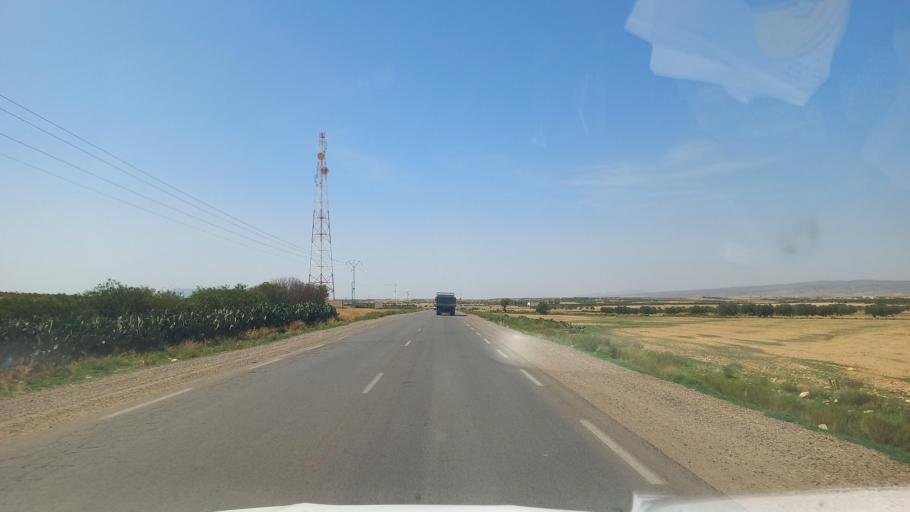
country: TN
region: Al Qasrayn
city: Sbiba
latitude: 35.3760
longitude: 9.1034
